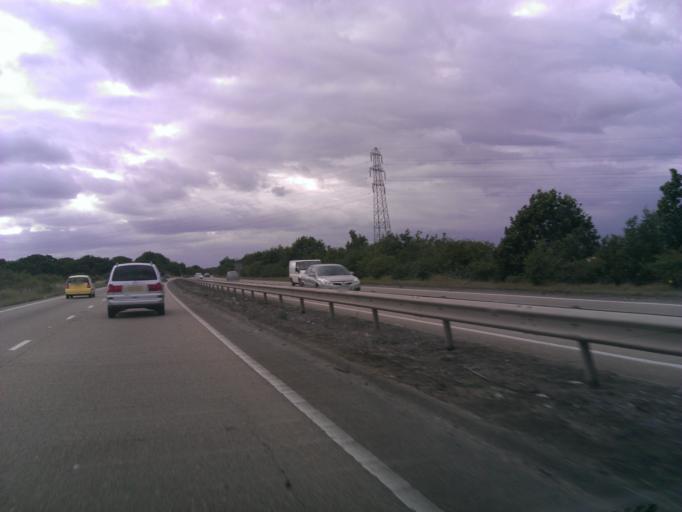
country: GB
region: England
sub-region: Essex
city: Alresford
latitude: 51.8986
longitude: 0.9879
